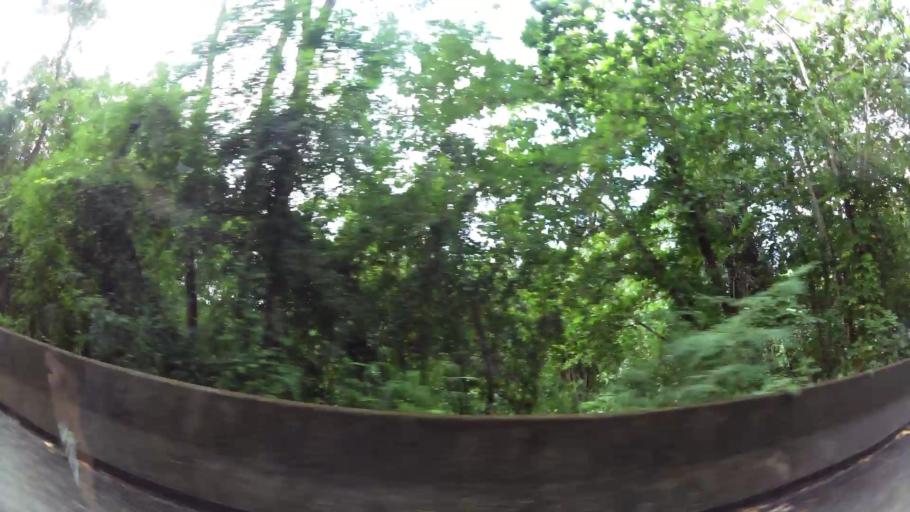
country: MQ
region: Martinique
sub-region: Martinique
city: Les Trois-Ilets
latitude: 14.4839
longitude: -61.0064
